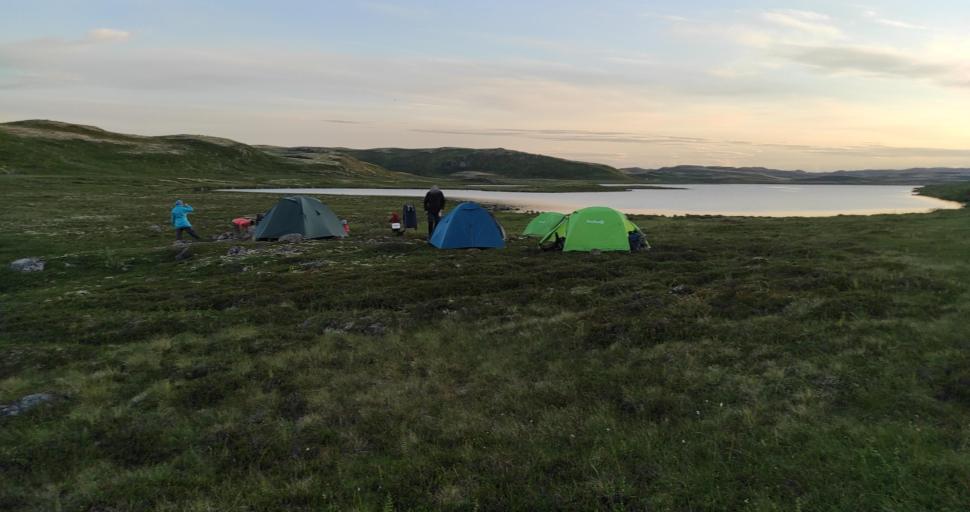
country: RU
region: Murmansk
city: Teriberka
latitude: 69.1702
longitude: 35.5147
